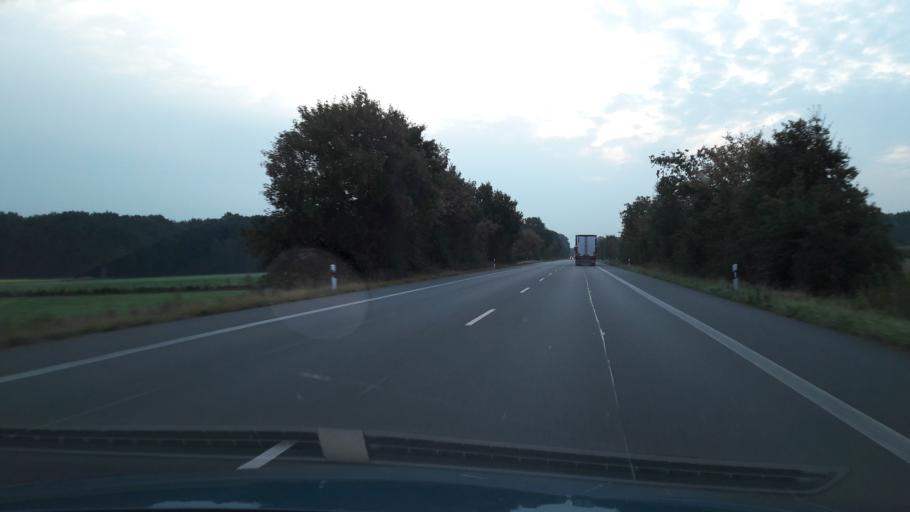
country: DE
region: North Rhine-Westphalia
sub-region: Regierungsbezirk Munster
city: Telgte
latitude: 51.9282
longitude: 7.7724
